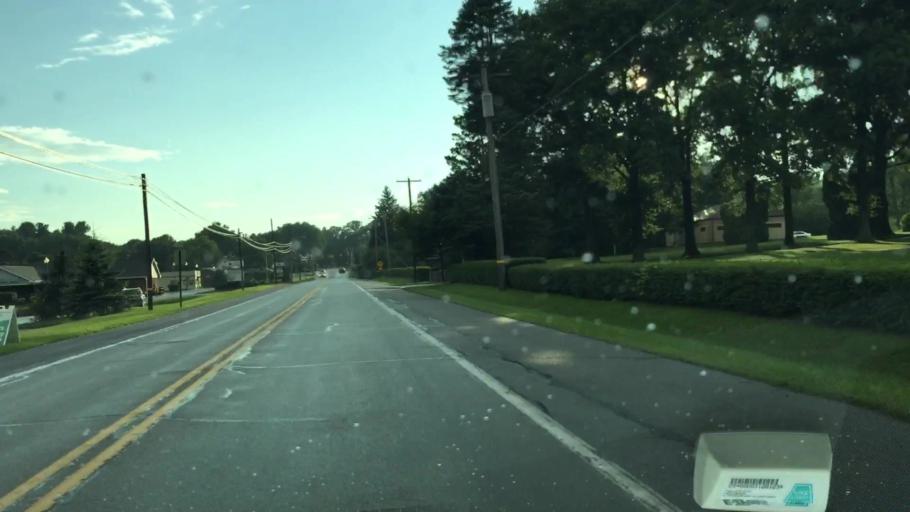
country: US
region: Pennsylvania
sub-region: Butler County
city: Meridian
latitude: 40.8671
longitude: -79.9506
